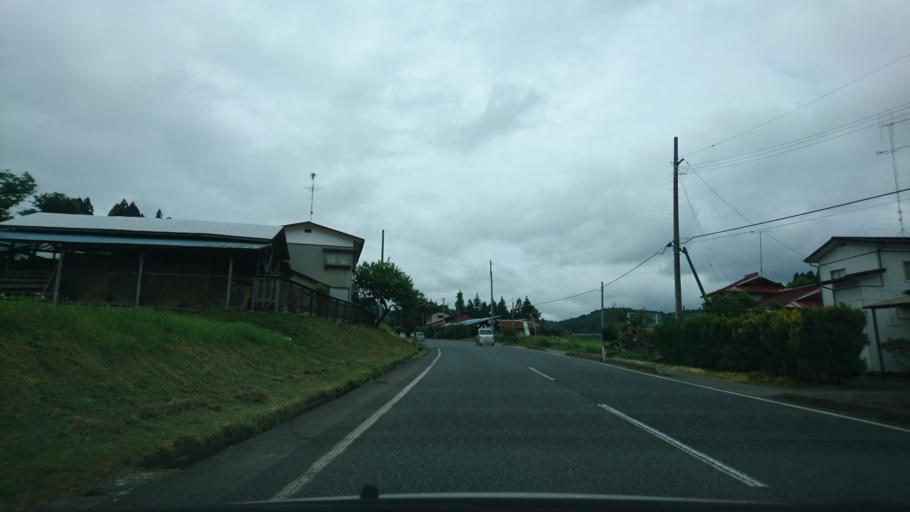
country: JP
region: Iwate
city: Ichinoseki
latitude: 38.8928
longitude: 141.1223
